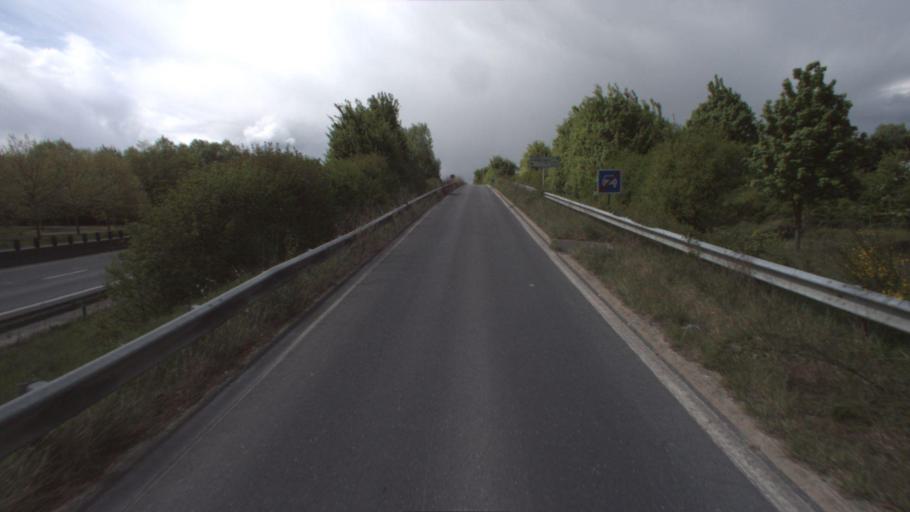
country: FR
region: Ile-de-France
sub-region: Departement de Seine-et-Marne
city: Tournan-en-Brie
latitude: 48.7339
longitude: 2.7800
